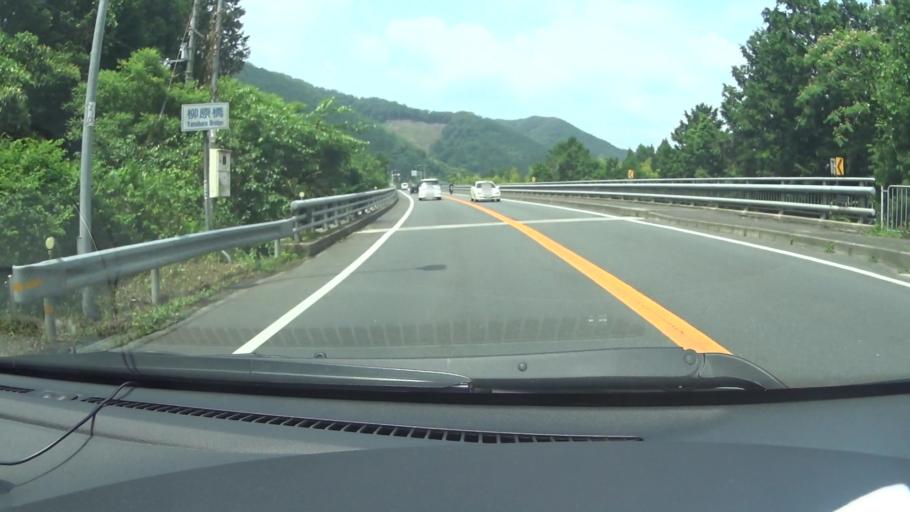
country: JP
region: Kyoto
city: Ayabe
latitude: 35.2684
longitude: 135.3729
